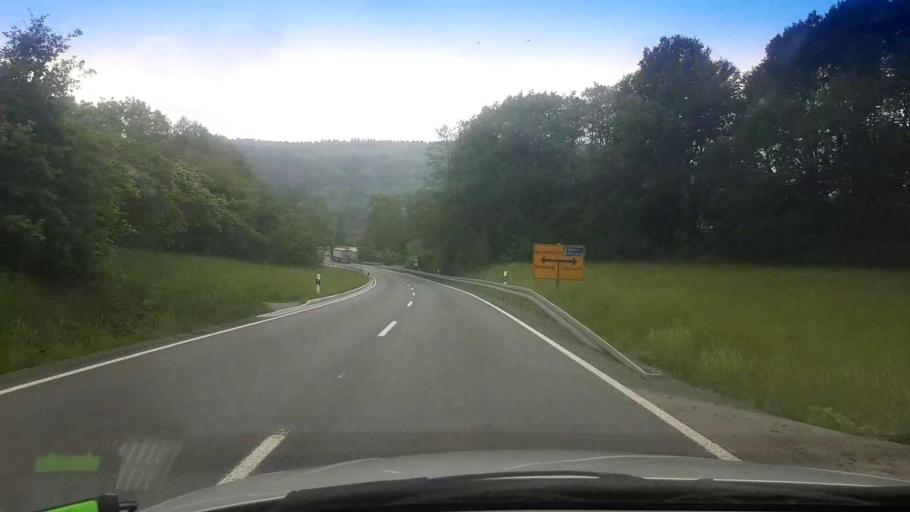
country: DE
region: Bavaria
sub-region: Upper Franconia
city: Reuth
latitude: 49.9717
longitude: 11.6908
